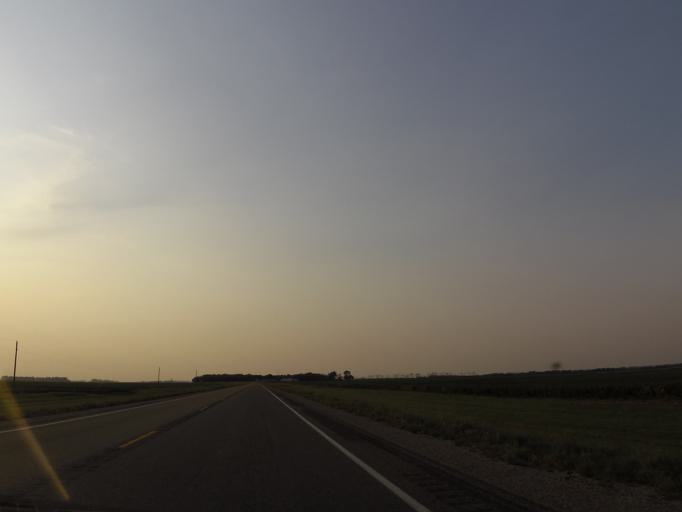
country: US
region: North Dakota
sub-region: Traill County
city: Mayville
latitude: 47.5071
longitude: -97.4145
